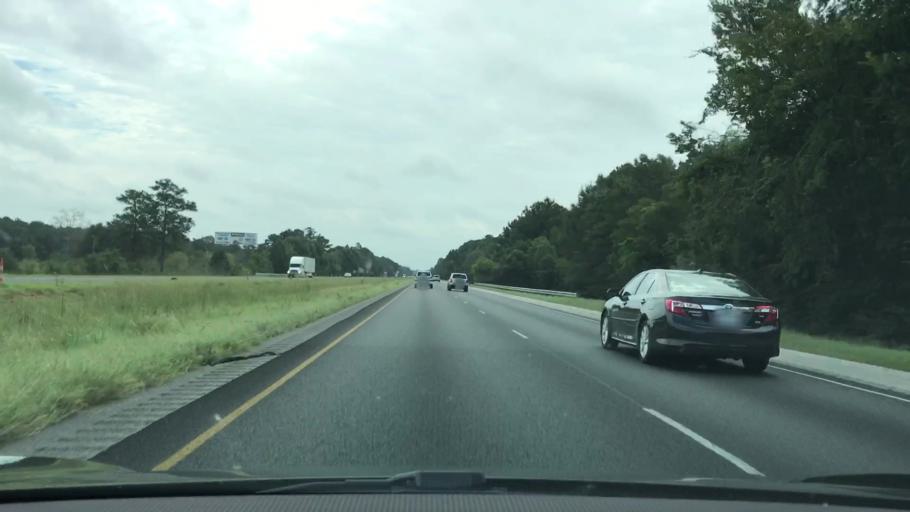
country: US
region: Alabama
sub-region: Montgomery County
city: Pike Road
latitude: 32.3737
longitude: -86.0352
